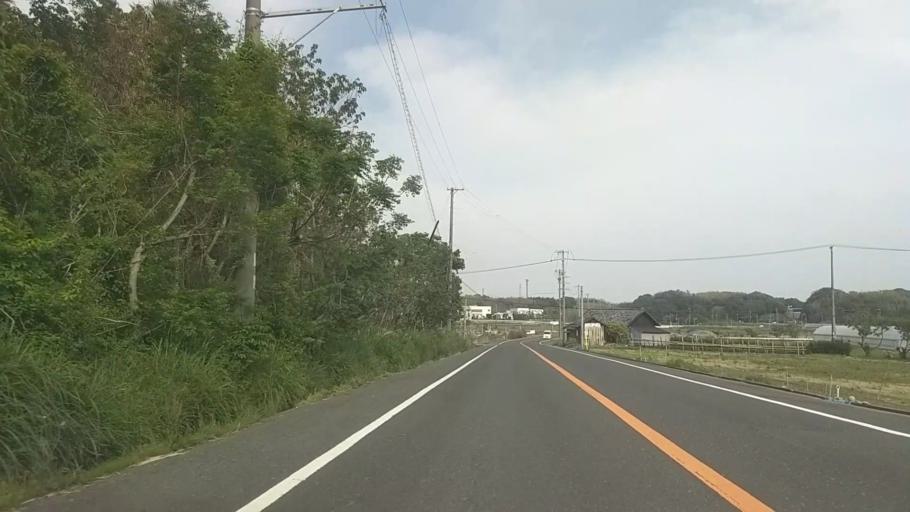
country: JP
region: Shizuoka
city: Kosai-shi
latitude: 34.7112
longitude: 137.6268
